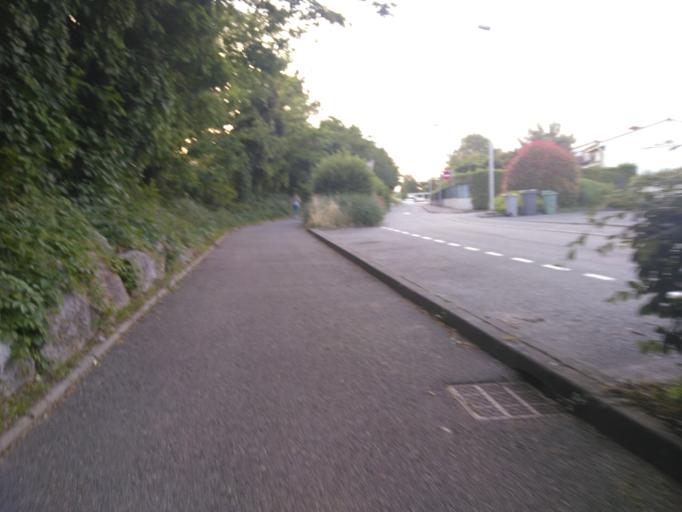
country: FR
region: Rhone-Alpes
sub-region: Departement de l'Isere
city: Voreppe
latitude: 45.2913
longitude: 5.6313
